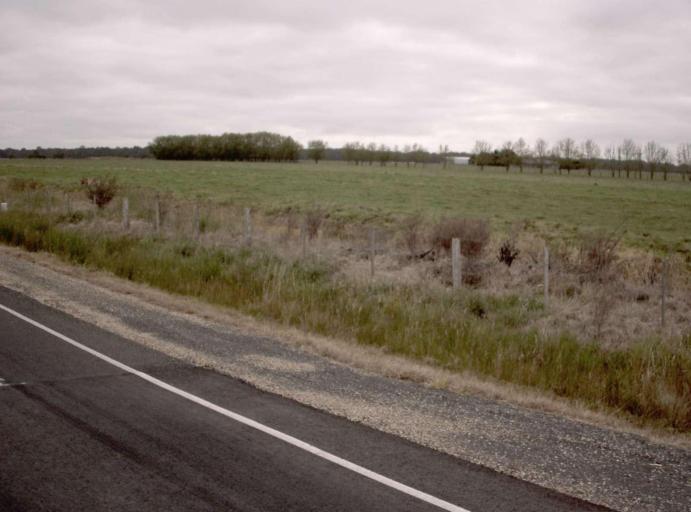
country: AU
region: Victoria
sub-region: Wellington
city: Sale
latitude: -38.0835
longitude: 146.9882
